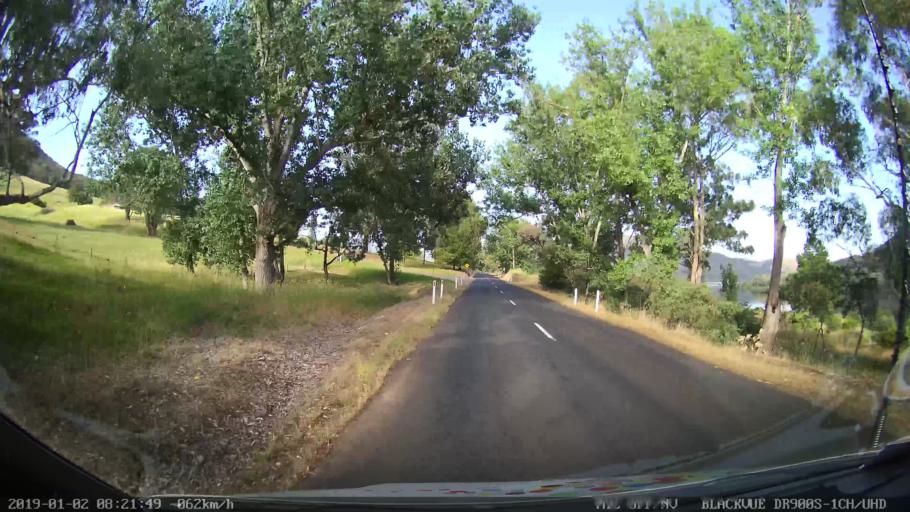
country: AU
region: New South Wales
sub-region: Tumut Shire
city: Tumut
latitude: -35.5689
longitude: 148.3225
